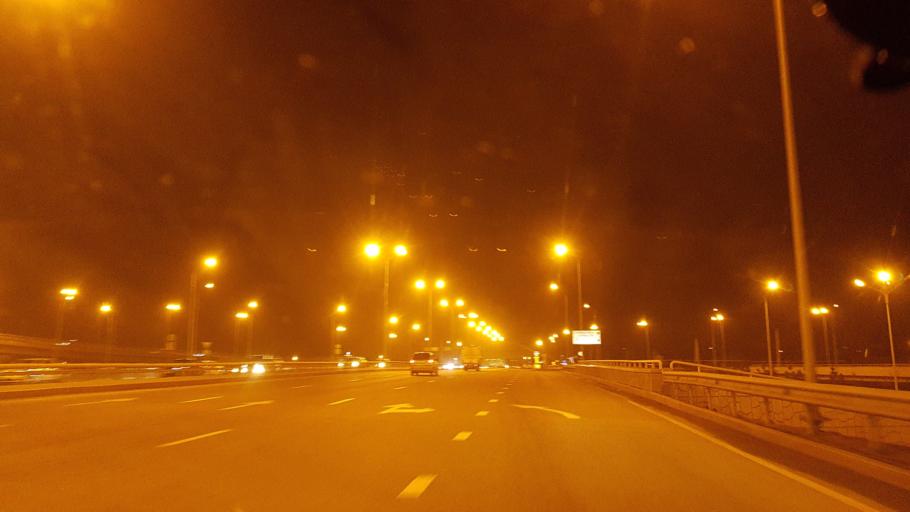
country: KZ
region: Almaty Qalasy
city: Almaty
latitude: 43.2567
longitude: 76.8394
